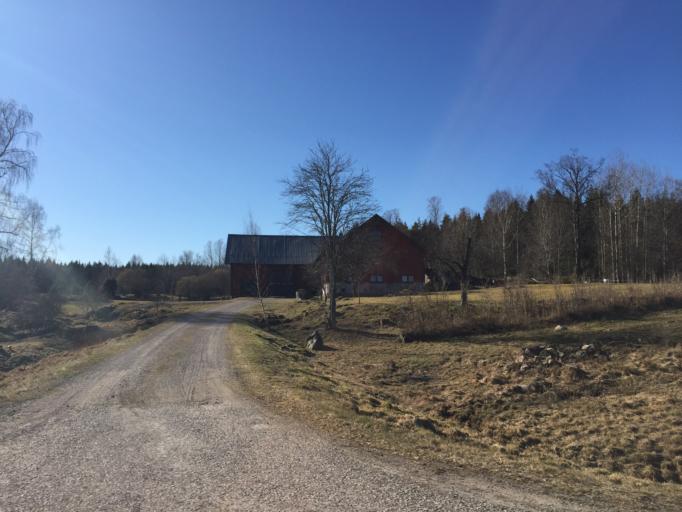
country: SE
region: OEstergoetland
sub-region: Finspangs Kommun
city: Finspang
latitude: 58.7815
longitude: 15.7710
